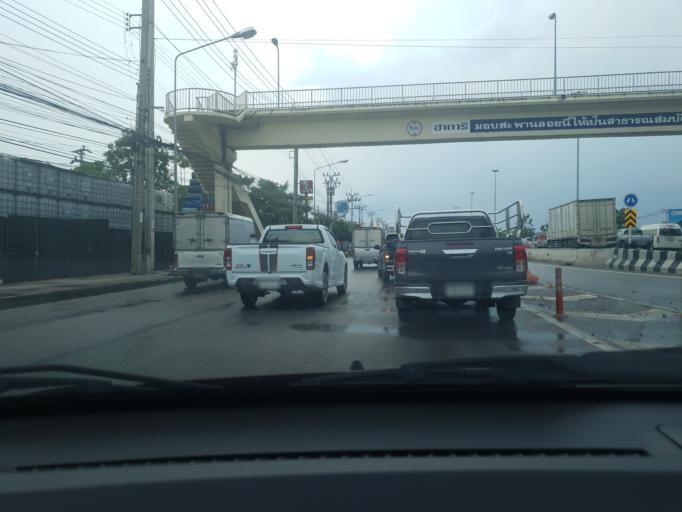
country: TH
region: Bangkok
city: Bang Bon
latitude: 13.6197
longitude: 100.3874
